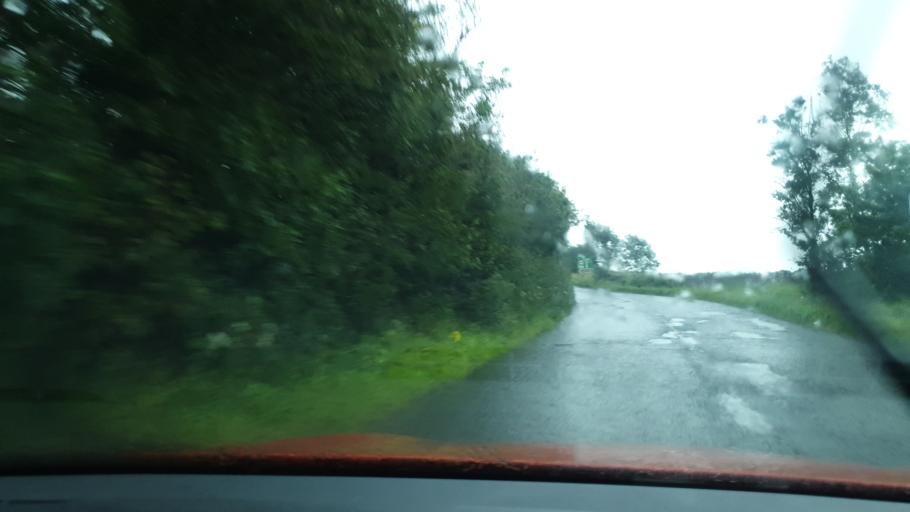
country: GB
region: England
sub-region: Cumbria
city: Millom
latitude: 54.2799
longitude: -3.2202
